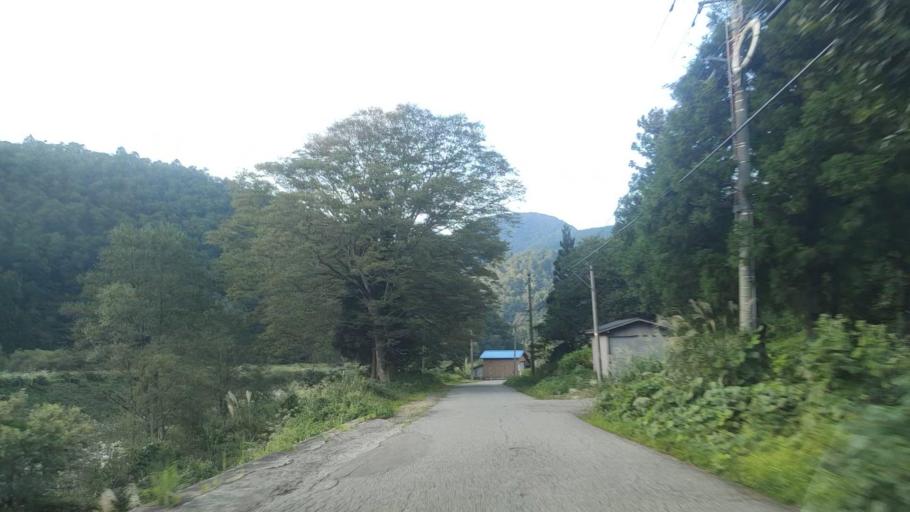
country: JP
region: Toyama
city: Yatsuomachi-higashikumisaka
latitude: 36.4718
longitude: 137.0854
